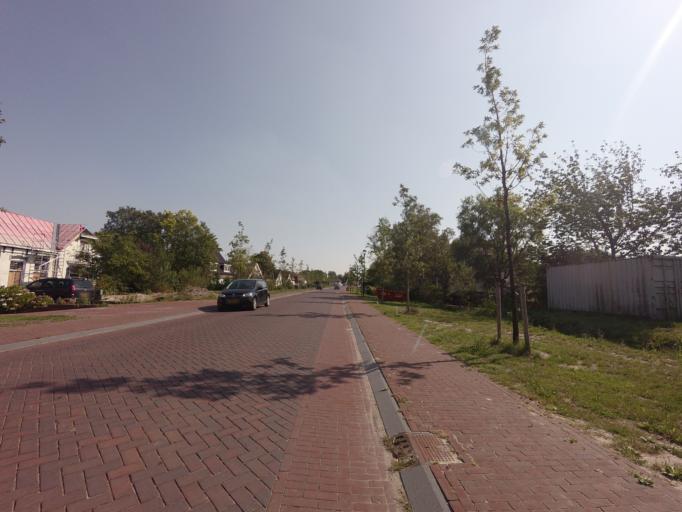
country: NL
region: Groningen
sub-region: Gemeente Zuidhorn
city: Noordhorn
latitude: 53.2569
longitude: 6.3983
